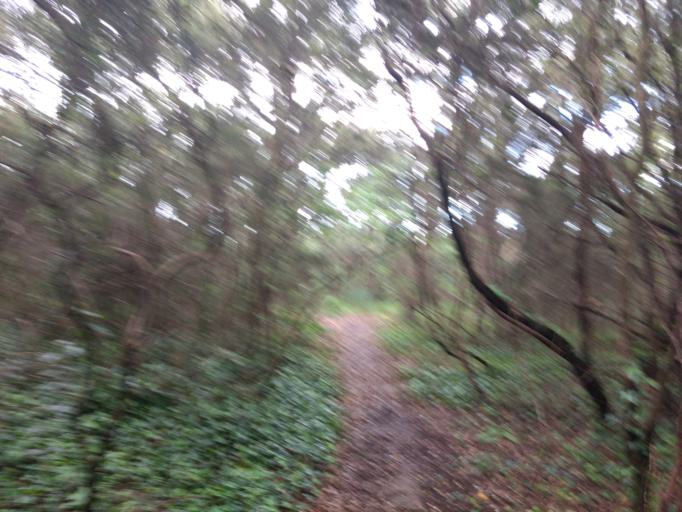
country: FR
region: Provence-Alpes-Cote d'Azur
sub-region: Departement des Alpes-Maritimes
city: Biot
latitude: 43.6216
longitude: 7.1225
